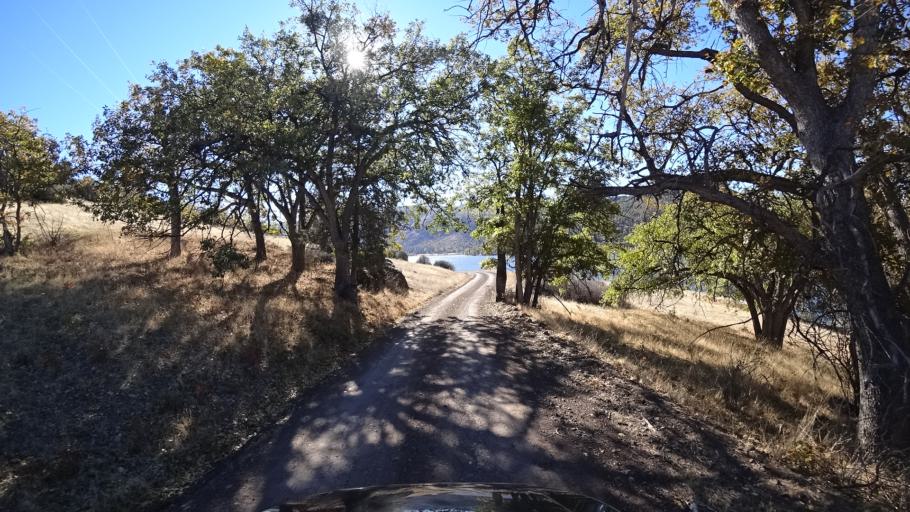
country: US
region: California
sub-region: Siskiyou County
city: Montague
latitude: 41.9819
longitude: -122.2945
